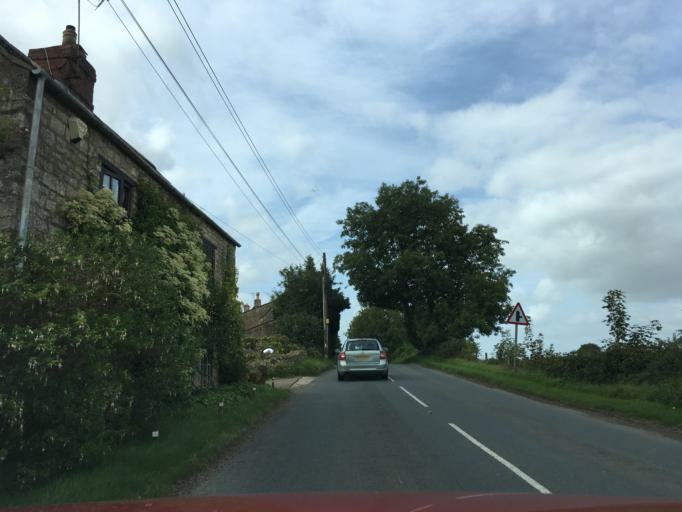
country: GB
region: England
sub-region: Gloucestershire
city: Stonehouse
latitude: 51.7002
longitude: -2.2926
